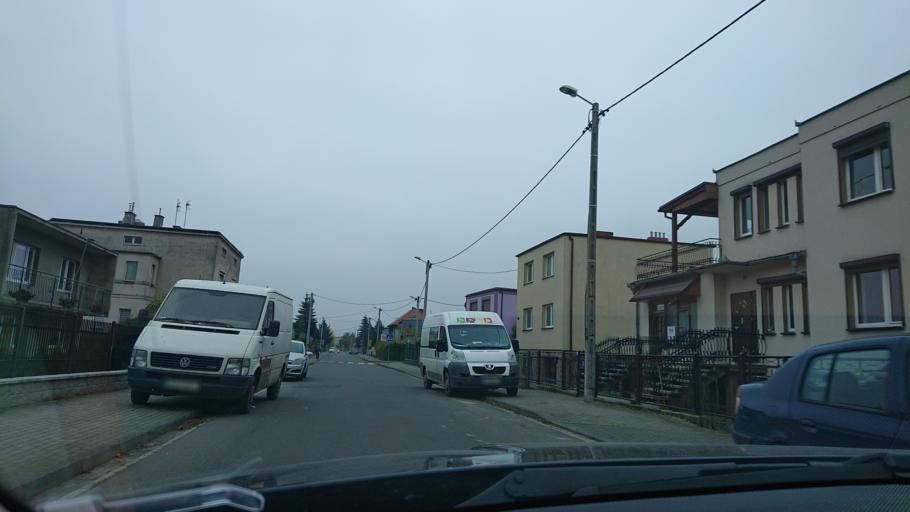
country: PL
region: Greater Poland Voivodeship
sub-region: Powiat gnieznienski
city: Gniezno
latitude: 52.5396
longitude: 17.6236
